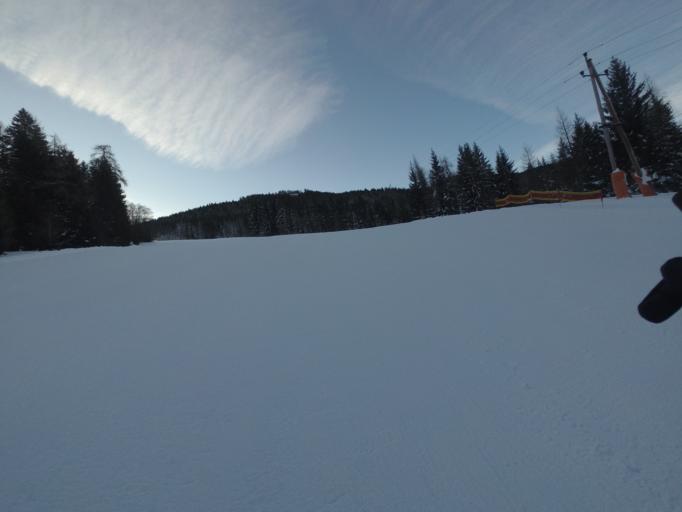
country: AT
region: Salzburg
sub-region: Politischer Bezirk Zell am See
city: Taxenbach
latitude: 47.2833
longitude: 13.0051
